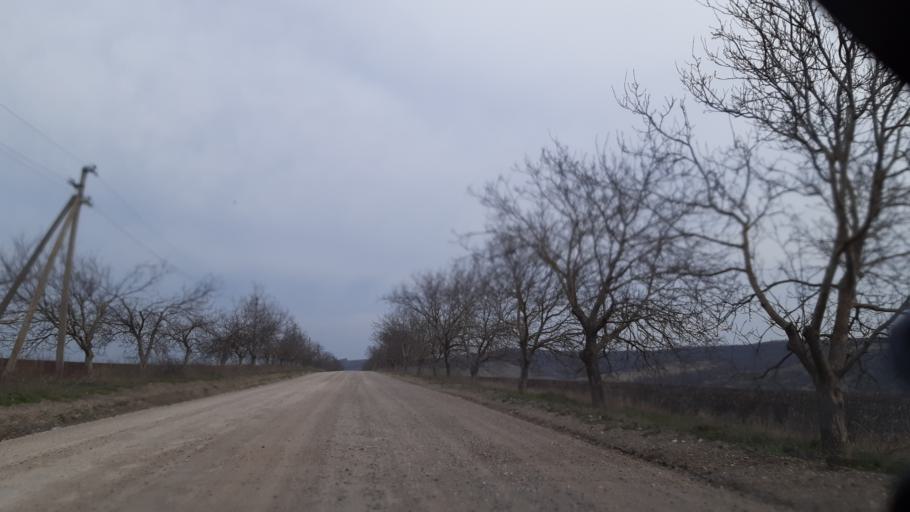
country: MD
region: Soldanesti
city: Soldanesti
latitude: 47.6935
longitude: 28.7356
